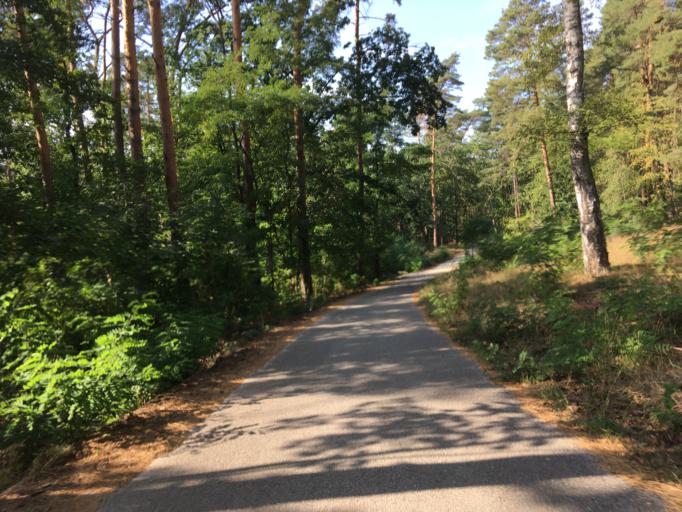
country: DE
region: Berlin
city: Muggelheim
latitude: 52.4099
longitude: 13.6410
